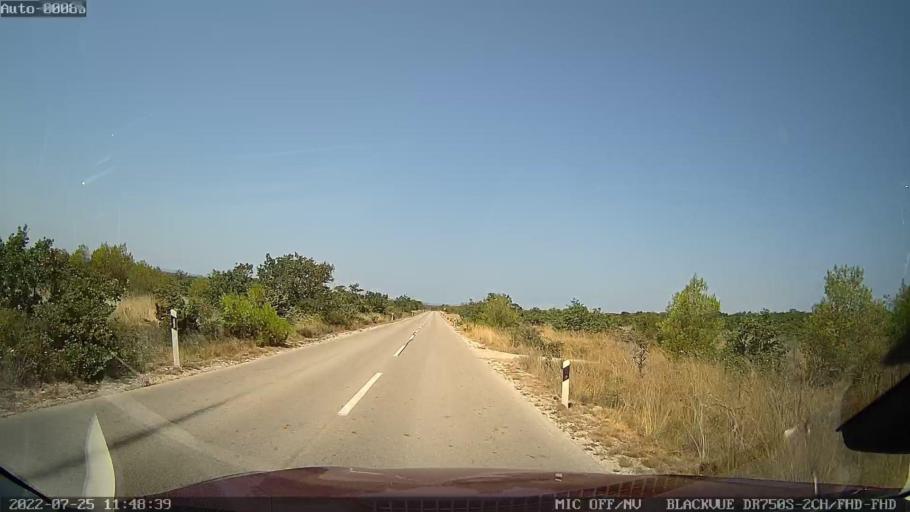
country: HR
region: Zadarska
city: Vrsi
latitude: 44.2340
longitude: 15.2951
